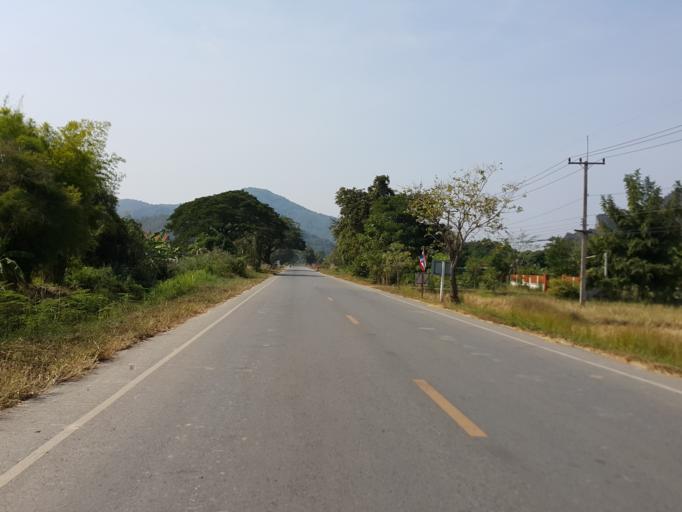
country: TH
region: Sukhothai
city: Thung Saliam
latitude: 17.3290
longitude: 99.5145
